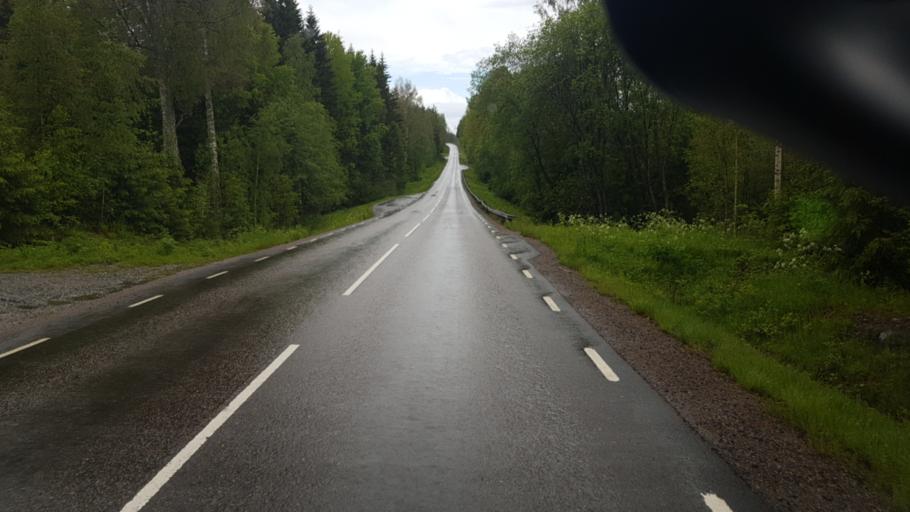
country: SE
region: Vaermland
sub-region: Eda Kommun
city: Amotfors
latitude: 59.7323
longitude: 12.4157
